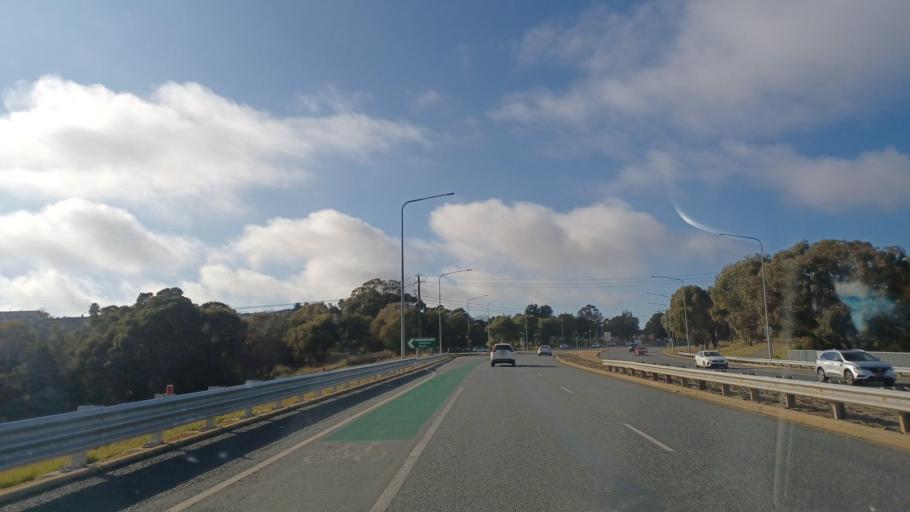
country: AU
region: Australian Capital Territory
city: Belconnen
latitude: -35.2223
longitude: 149.0688
